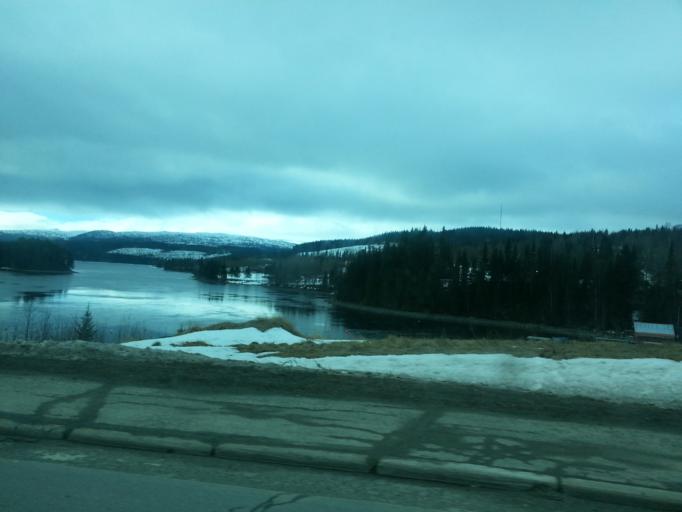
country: NO
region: Nord-Trondelag
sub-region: Lierne
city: Sandvika
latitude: 64.4985
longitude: 14.1454
